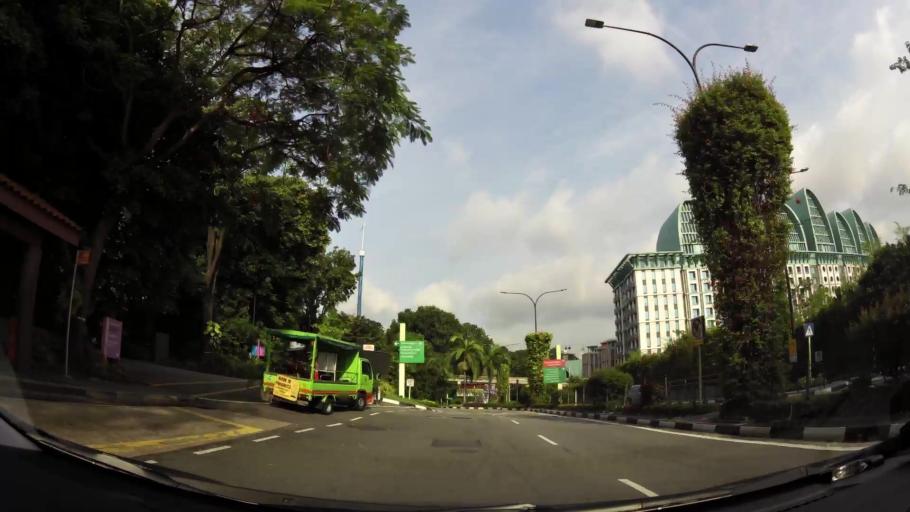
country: SG
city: Singapore
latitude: 1.2537
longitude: 103.8204
